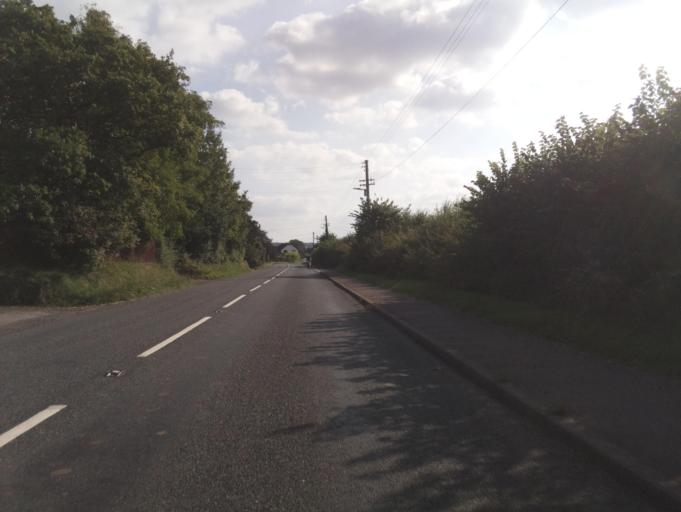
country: GB
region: England
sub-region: Devon
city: Heavitree
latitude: 50.7892
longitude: -3.4940
